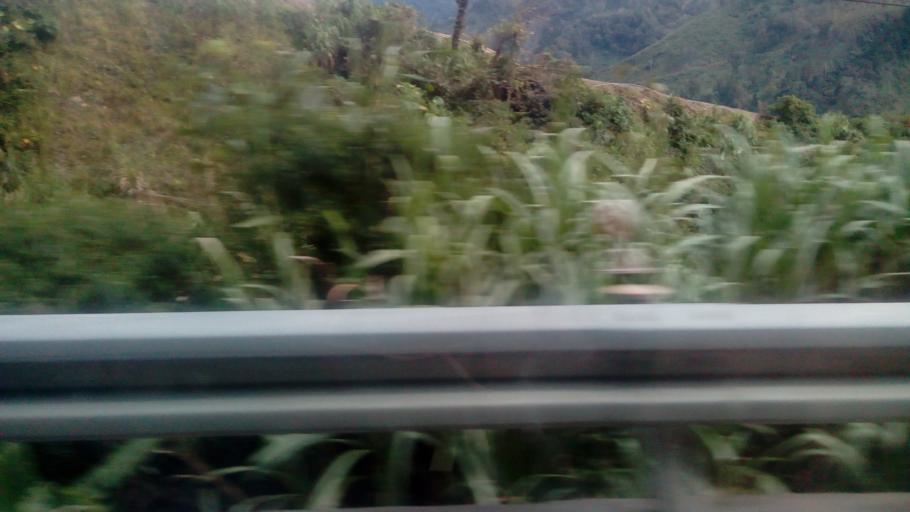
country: TW
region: Taiwan
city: Daxi
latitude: 24.4567
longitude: 121.3937
